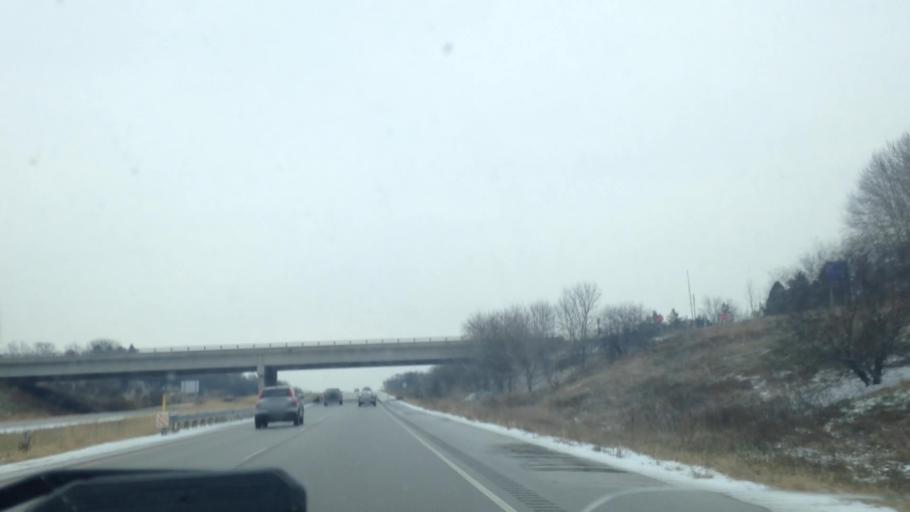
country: US
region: Wisconsin
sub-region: Waukesha County
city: Nashotah
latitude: 43.1016
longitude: -88.4051
